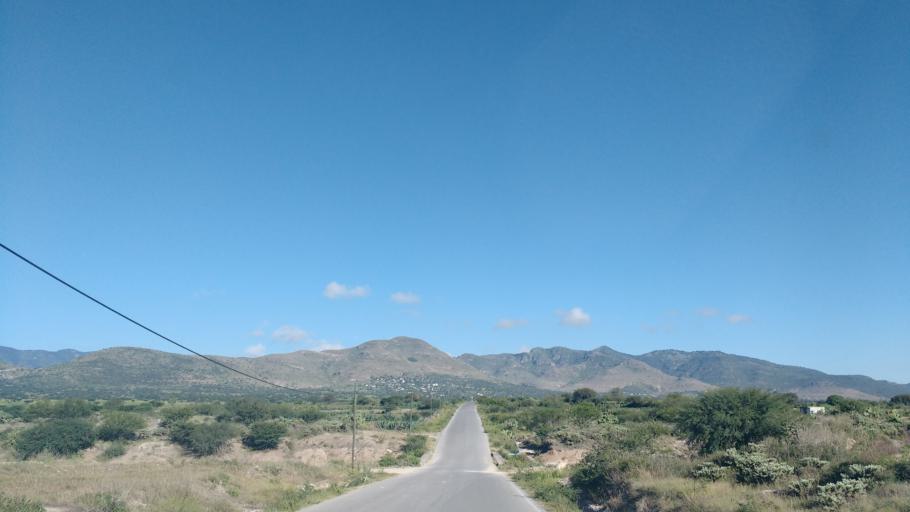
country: MX
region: Hidalgo
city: Mixquiahuala de Juarez
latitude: 20.2549
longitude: -99.2516
